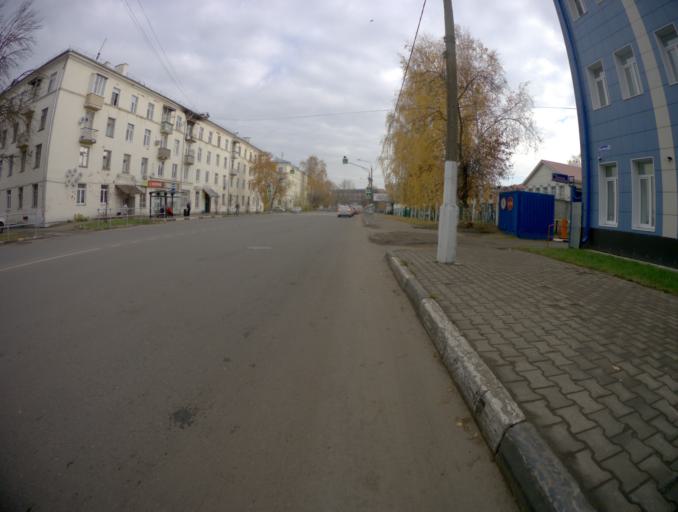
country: RU
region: Moskovskaya
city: Orekhovo-Zuyevo
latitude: 55.8045
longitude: 38.9670
